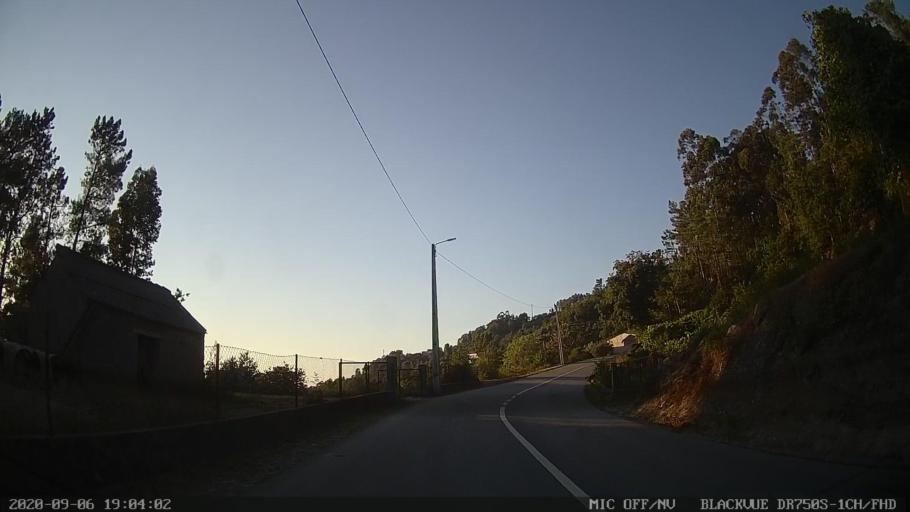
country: PT
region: Porto
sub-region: Baiao
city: Baiao
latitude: 41.2290
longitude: -7.9957
